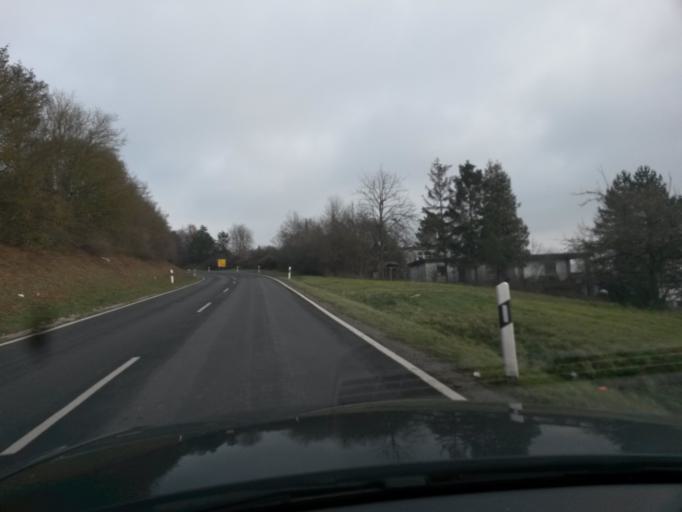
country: DE
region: Bavaria
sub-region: Regierungsbezirk Unterfranken
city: Kurnach
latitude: 49.8443
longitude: 10.0239
